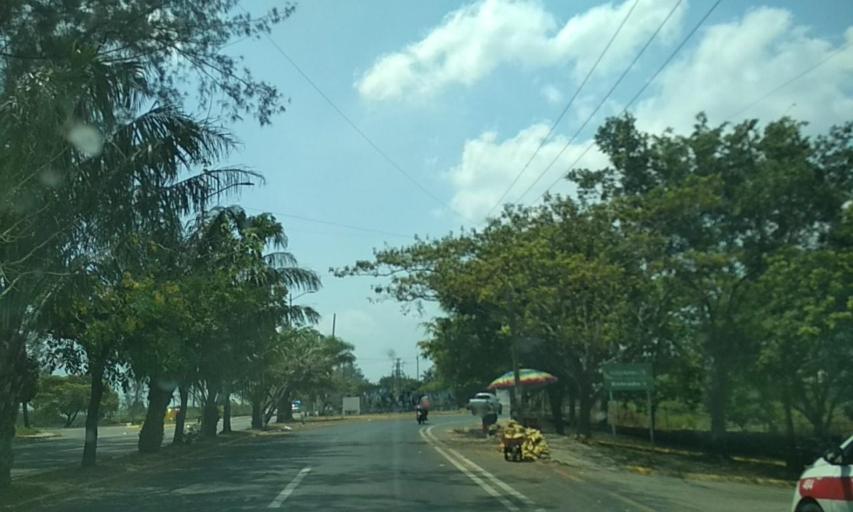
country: MX
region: Veracruz
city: Las Choapas
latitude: 17.9303
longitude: -94.0969
